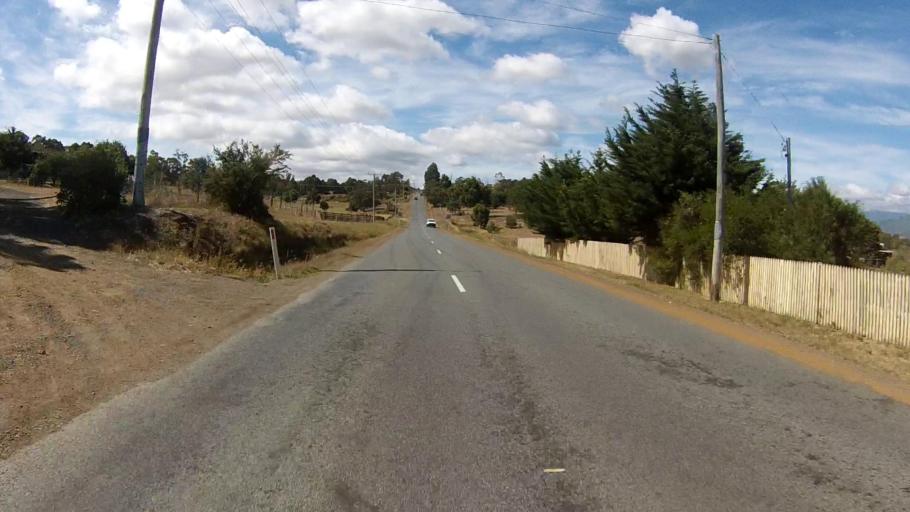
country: AU
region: Tasmania
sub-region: Brighton
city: Bridgewater
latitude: -42.7105
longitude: 147.2699
